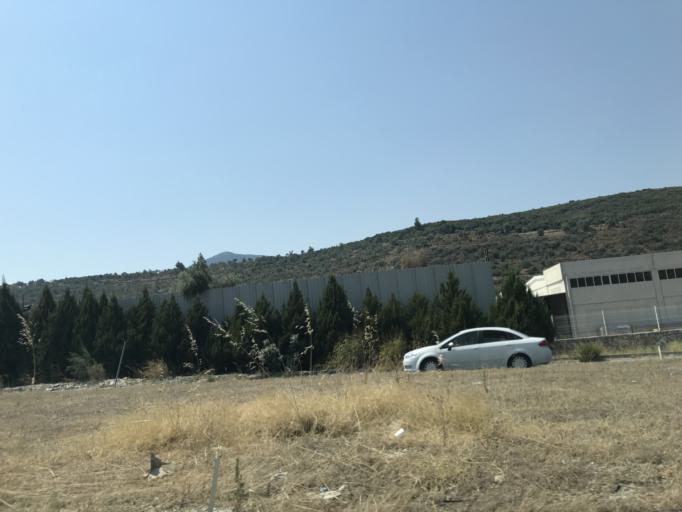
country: TR
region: Mugla
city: Milas
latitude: 37.3372
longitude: 27.7578
